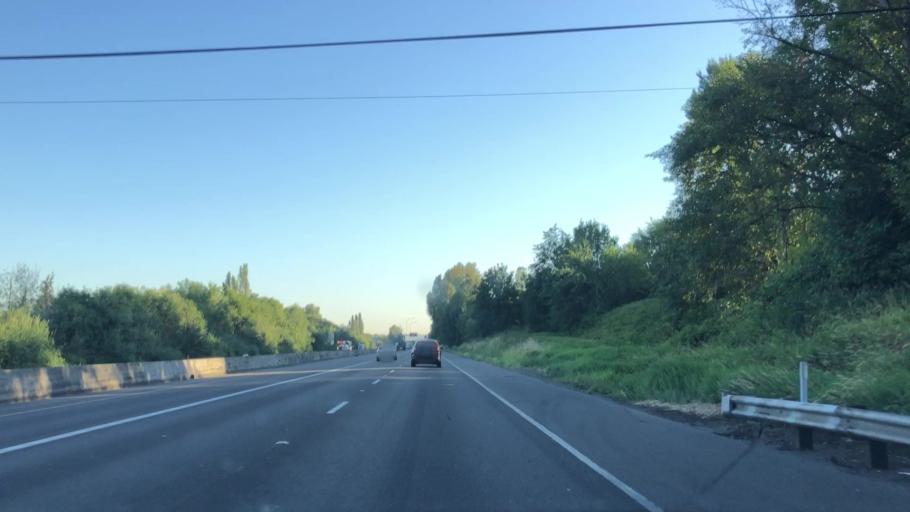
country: US
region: Washington
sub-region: King County
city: Kent
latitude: 47.4156
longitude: -122.2207
